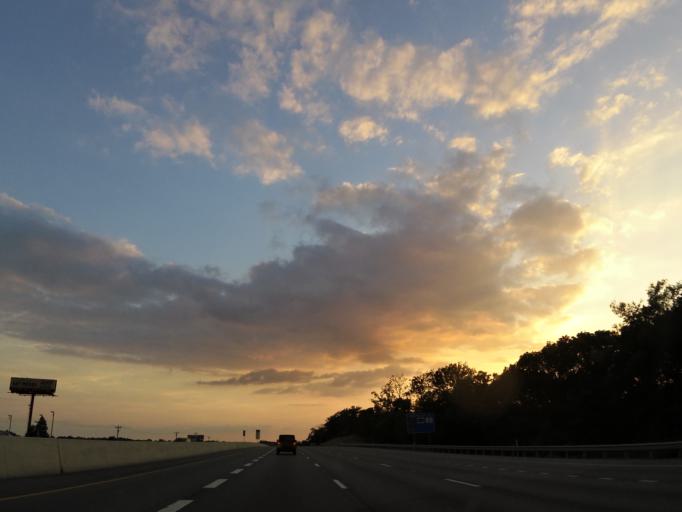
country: US
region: Tennessee
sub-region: Wilson County
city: Mount Juliet
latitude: 36.1757
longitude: -86.4792
